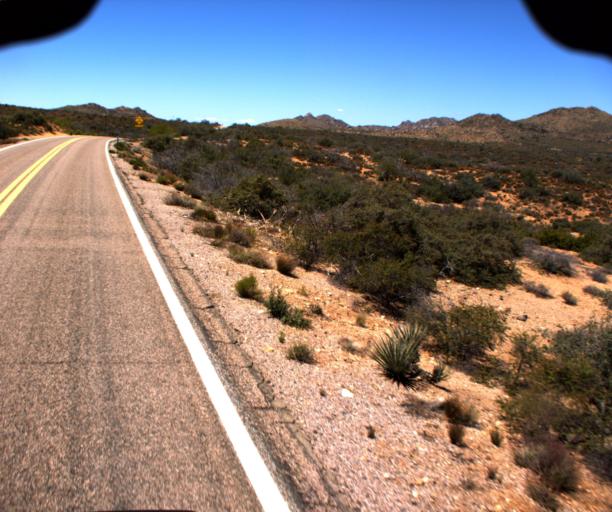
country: US
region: Arizona
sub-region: Yavapai County
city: Congress
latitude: 34.4335
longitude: -112.9230
